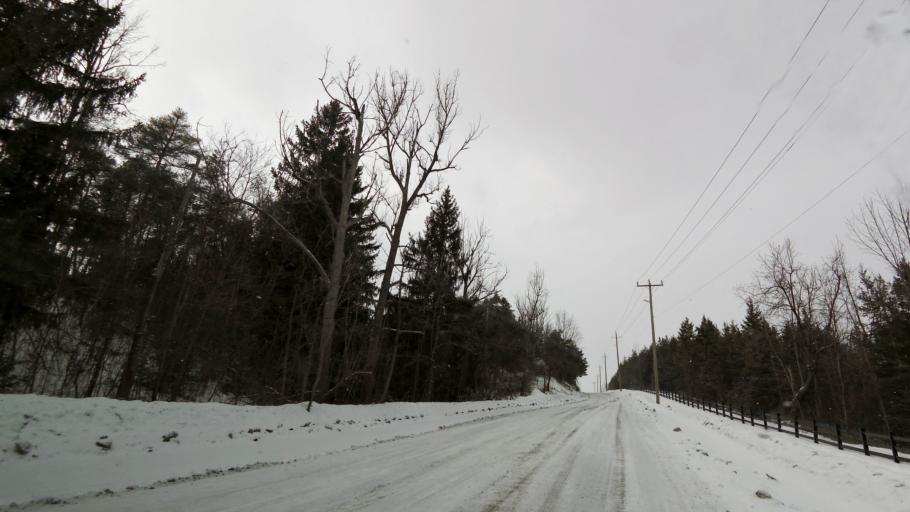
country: CA
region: Ontario
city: Orangeville
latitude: 43.8312
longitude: -79.9803
